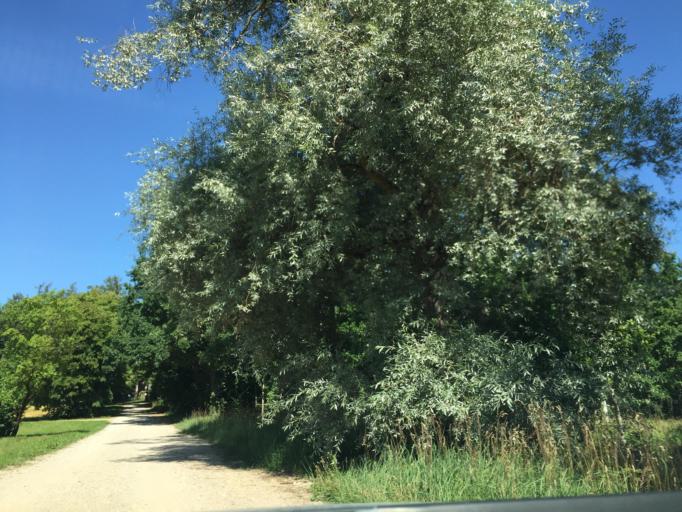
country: LV
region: Talsu Rajons
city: Talsi
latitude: 57.2276
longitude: 22.5264
